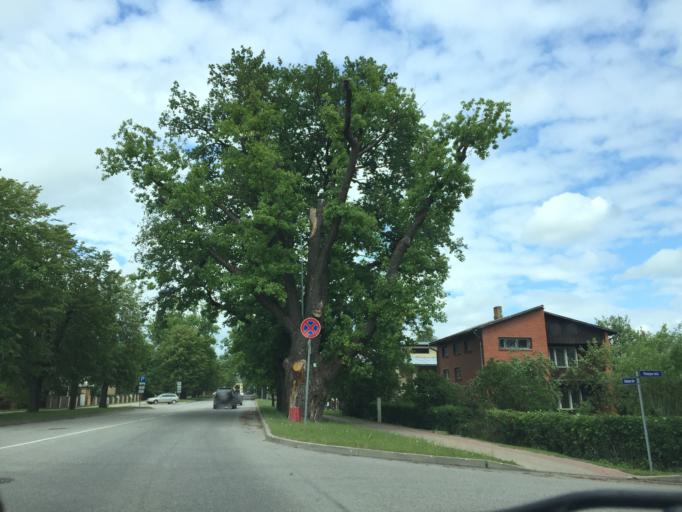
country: LV
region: Valmieras Rajons
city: Valmiera
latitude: 57.5461
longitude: 25.4316
